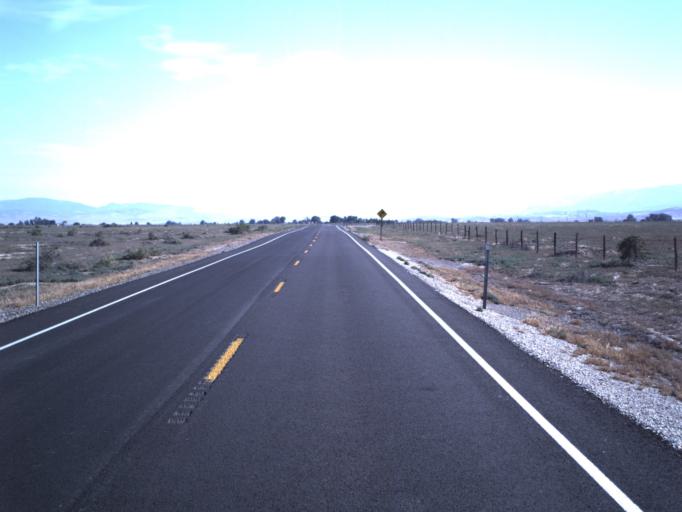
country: US
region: Utah
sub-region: Sevier County
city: Salina
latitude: 39.0311
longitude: -111.8414
